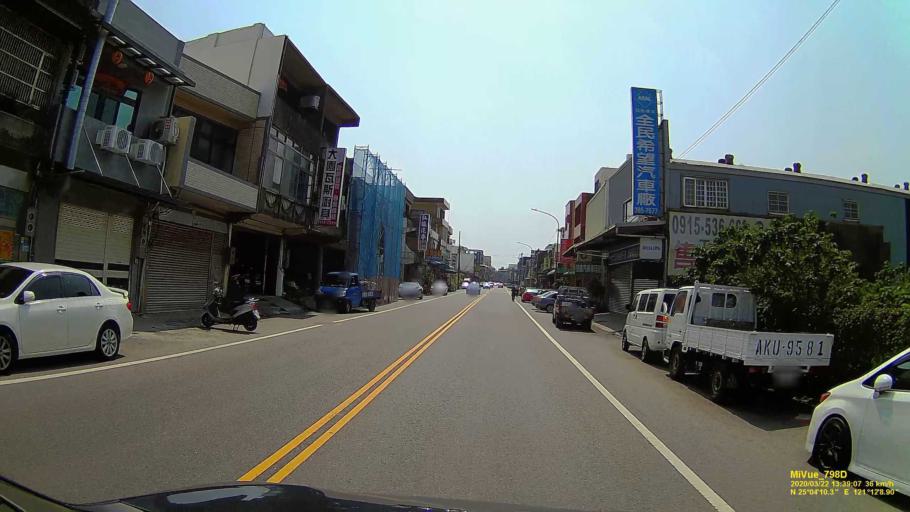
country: TW
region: Taiwan
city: Taoyuan City
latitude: 25.0694
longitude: 121.2023
